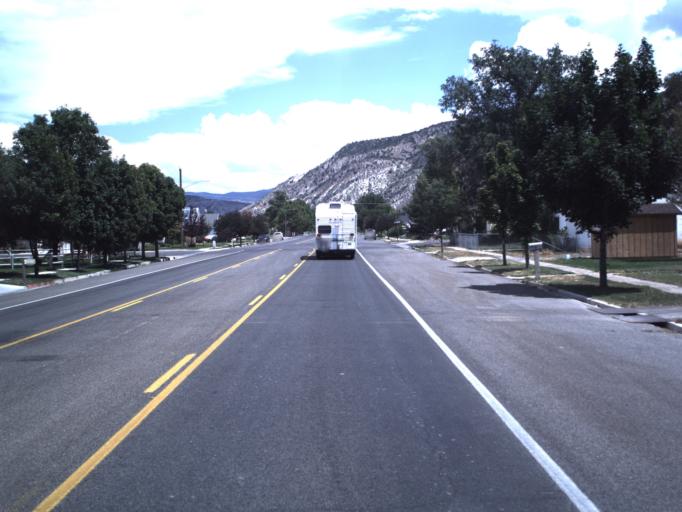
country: US
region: Utah
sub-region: Juab County
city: Nephi
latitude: 39.7100
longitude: -111.8335
